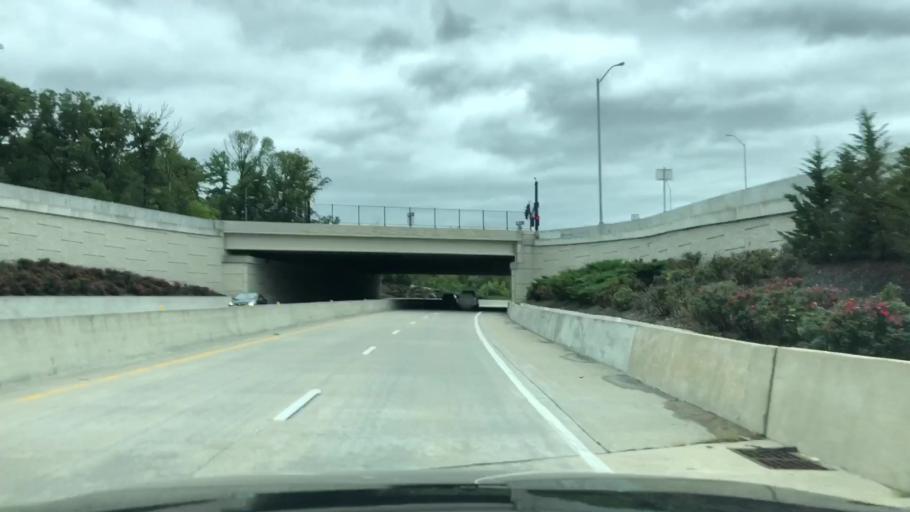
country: US
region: Missouri
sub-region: Saint Louis County
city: Town and Country
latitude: 38.6612
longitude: -90.5033
